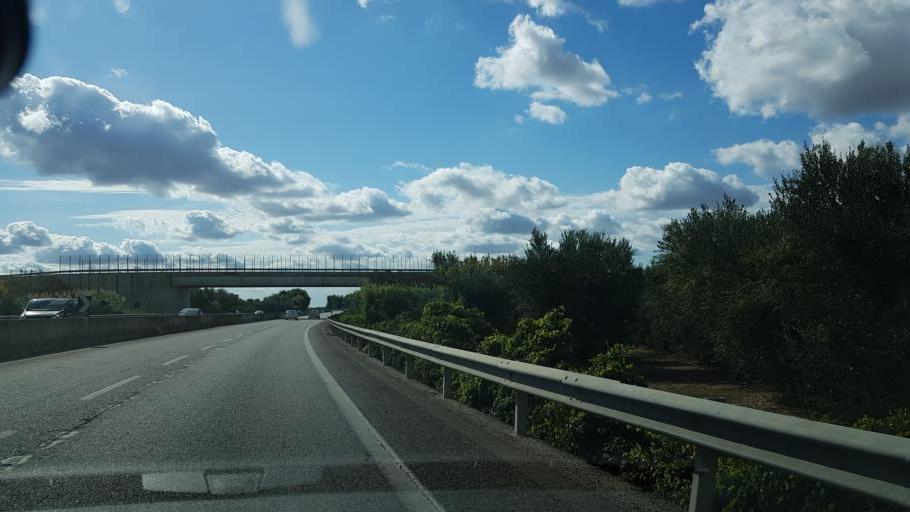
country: IT
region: Apulia
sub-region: Provincia di Brindisi
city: San Pietro Vernotico
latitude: 40.5116
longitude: 18.0235
